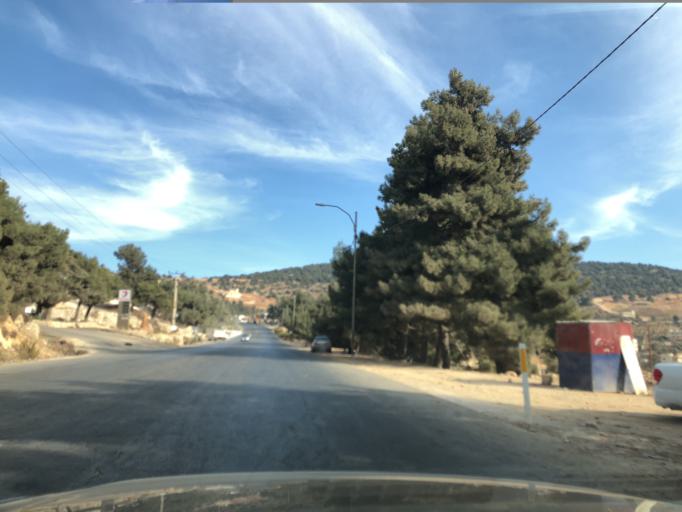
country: JO
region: Irbid
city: `Anjarah
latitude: 32.3143
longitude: 35.7726
